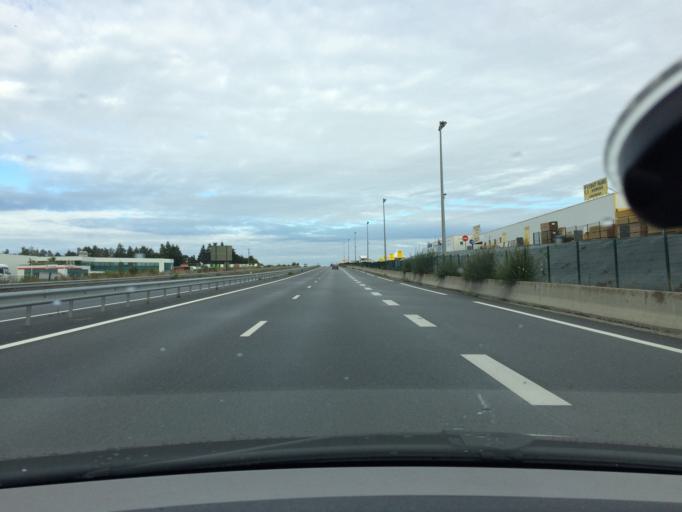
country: FR
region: Brittany
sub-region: Departement d'Ille-et-Vilaine
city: Janze
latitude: 47.9721
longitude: -1.5396
